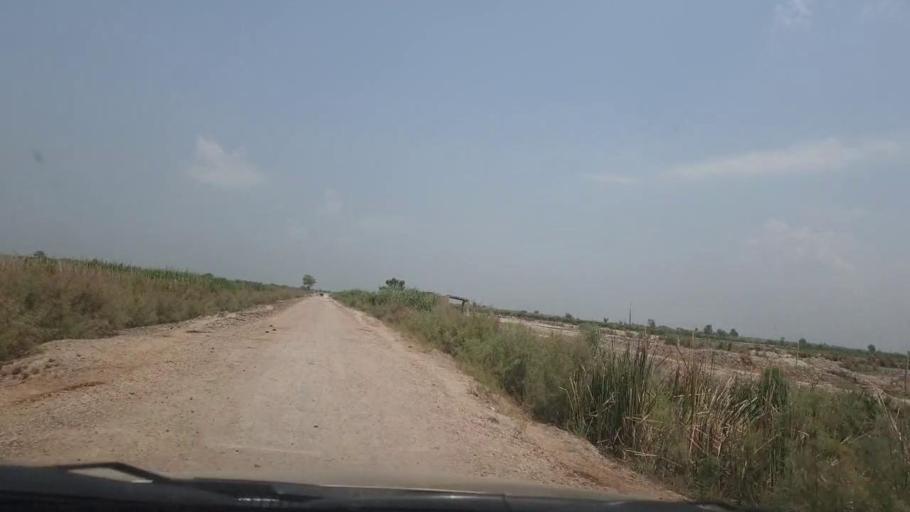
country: PK
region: Sindh
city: Ratodero
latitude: 27.7146
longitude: 68.2869
